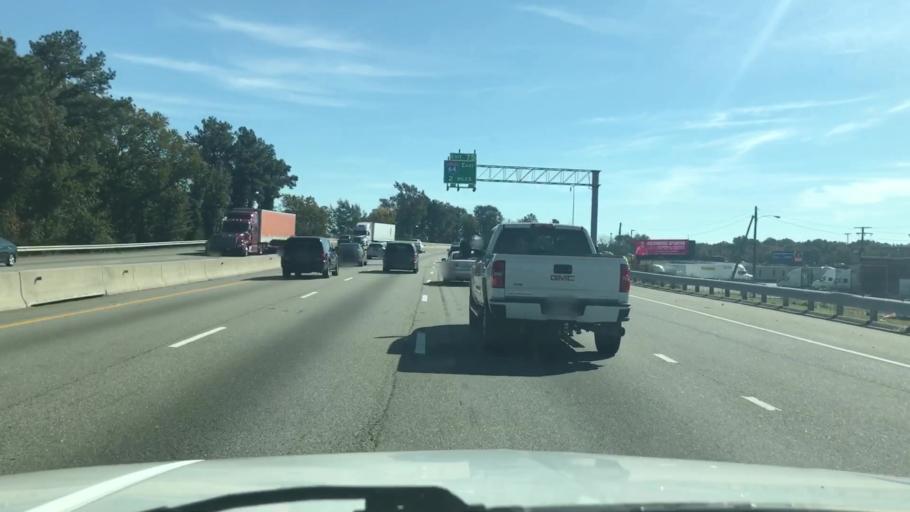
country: US
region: Virginia
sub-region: City of Richmond
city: Richmond
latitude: 37.5723
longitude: -77.4567
